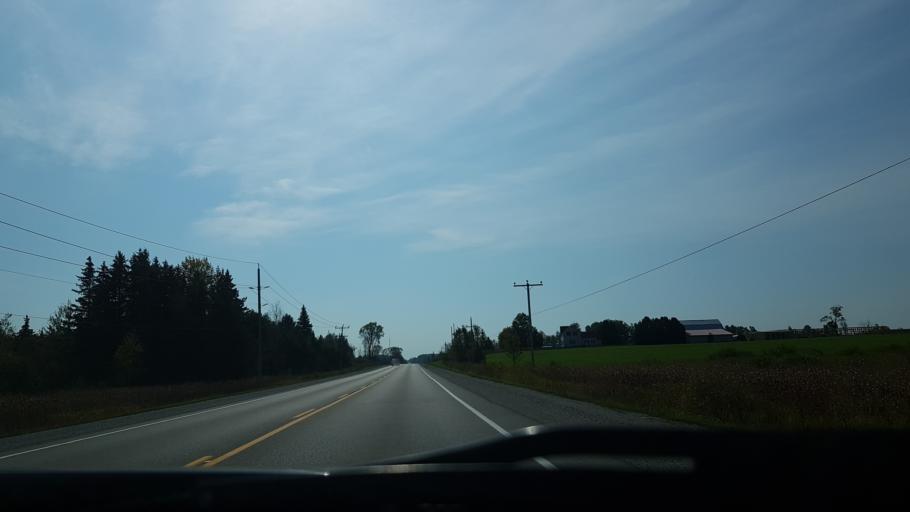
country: CA
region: Ontario
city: Orillia
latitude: 44.7087
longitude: -79.2795
